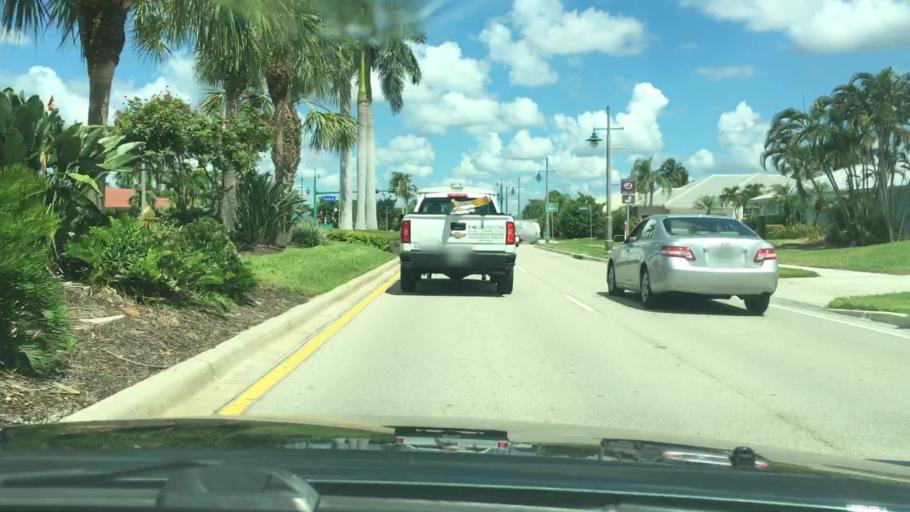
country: US
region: Florida
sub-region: Collier County
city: Marco
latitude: 25.9466
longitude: -81.7327
